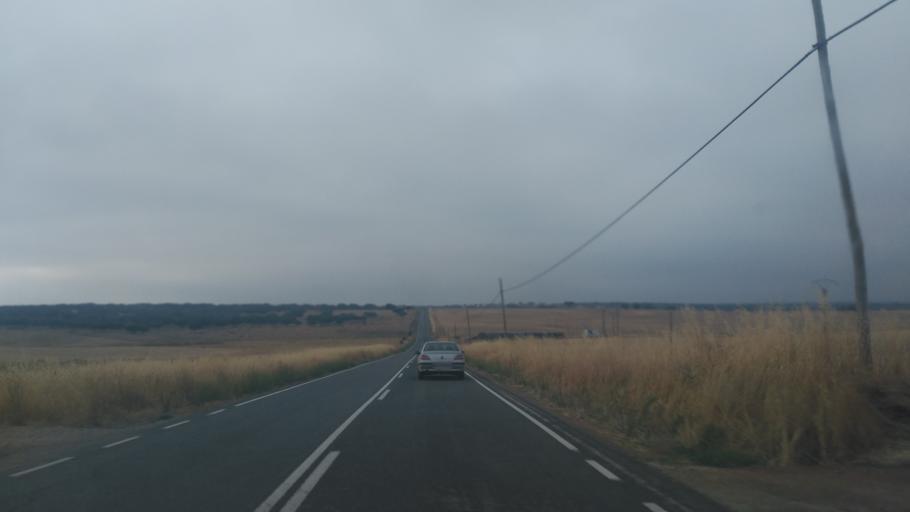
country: ES
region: Castille and Leon
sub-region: Provincia de Salamanca
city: Robliza de Cojos
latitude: 40.8620
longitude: -5.9660
